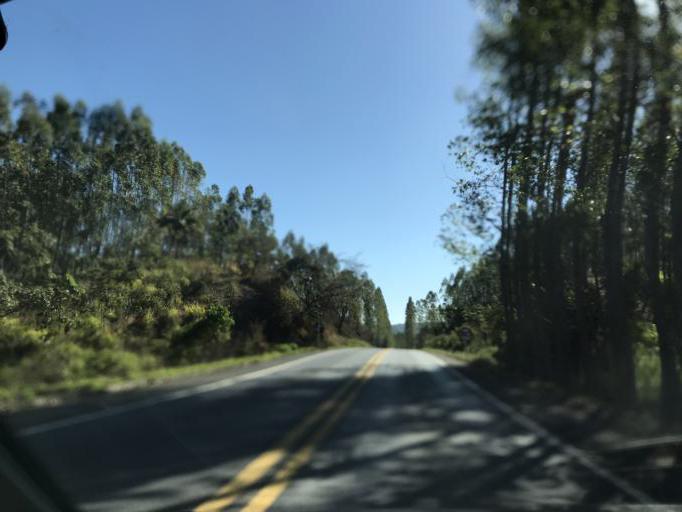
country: BR
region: Minas Gerais
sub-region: Bambui
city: Bambui
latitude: -19.8235
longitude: -46.0129
